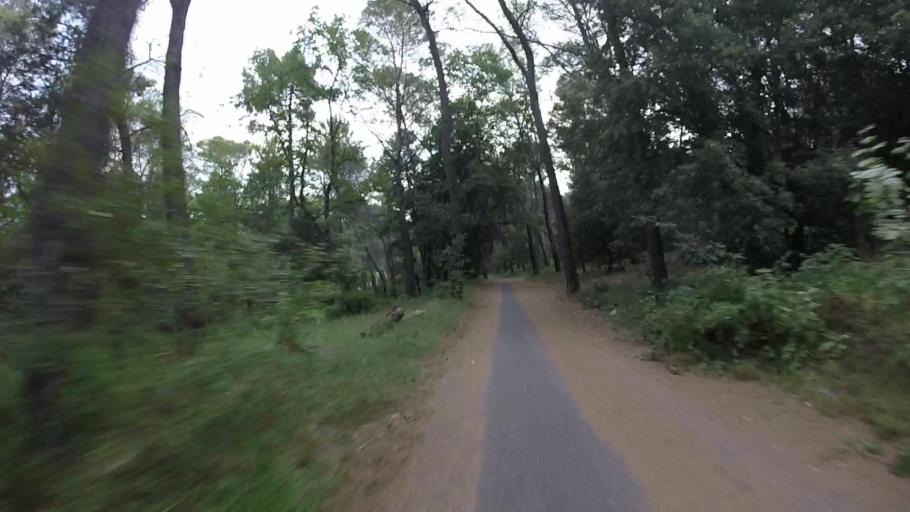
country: FR
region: Provence-Alpes-Cote d'Azur
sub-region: Departement des Alpes-Maritimes
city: Vallauris
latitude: 43.6122
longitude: 7.0440
